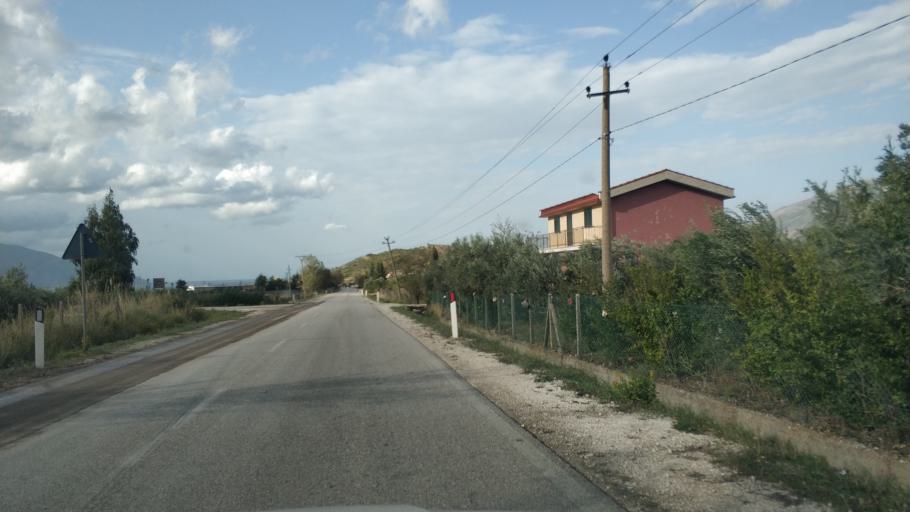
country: AL
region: Vlore
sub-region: Rrethi i Vlores
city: Orikum
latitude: 40.2894
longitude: 19.4930
